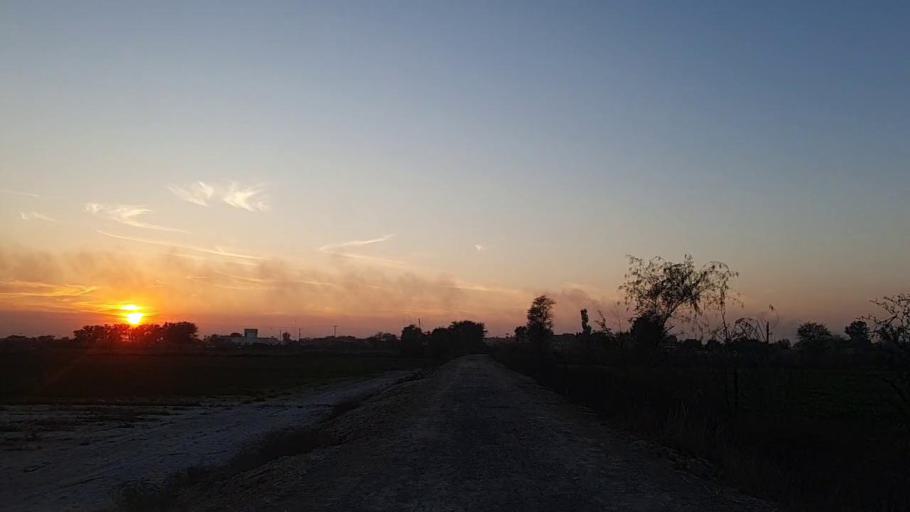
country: PK
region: Sindh
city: Bandhi
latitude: 26.5976
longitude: 68.3397
